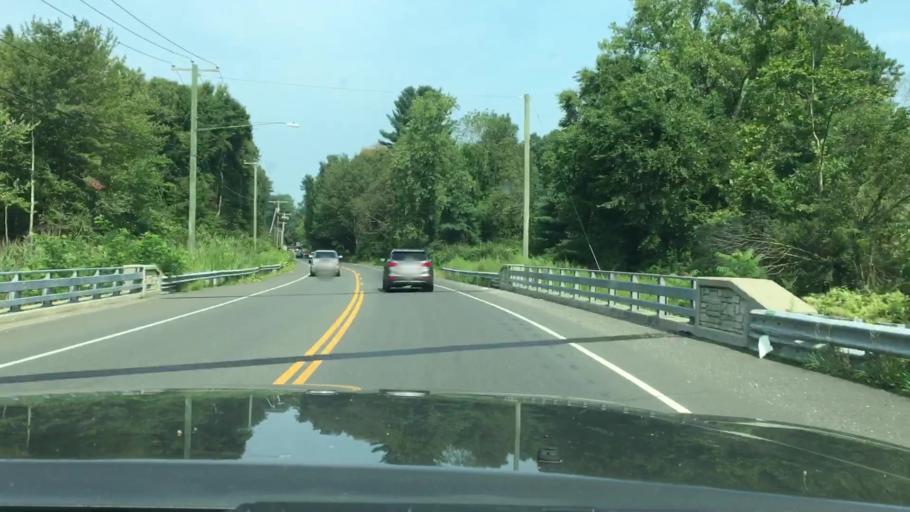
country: US
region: Connecticut
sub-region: Fairfield County
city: Georgetown
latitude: 41.2929
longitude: -73.4511
